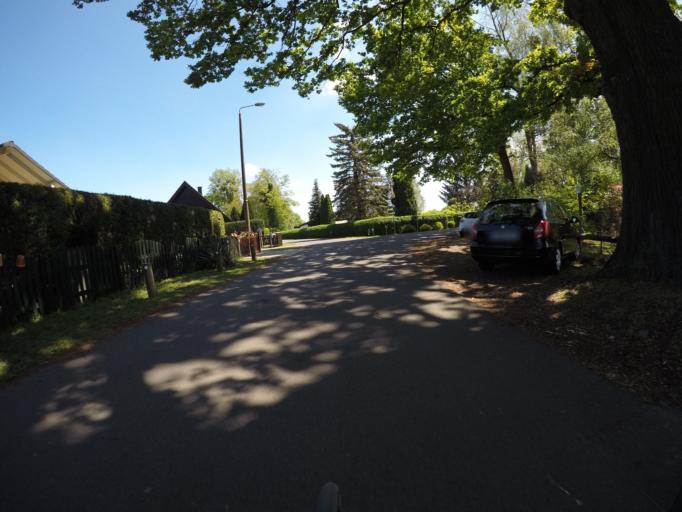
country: DE
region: Brandenburg
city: Werder
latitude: 52.4297
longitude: 12.9533
